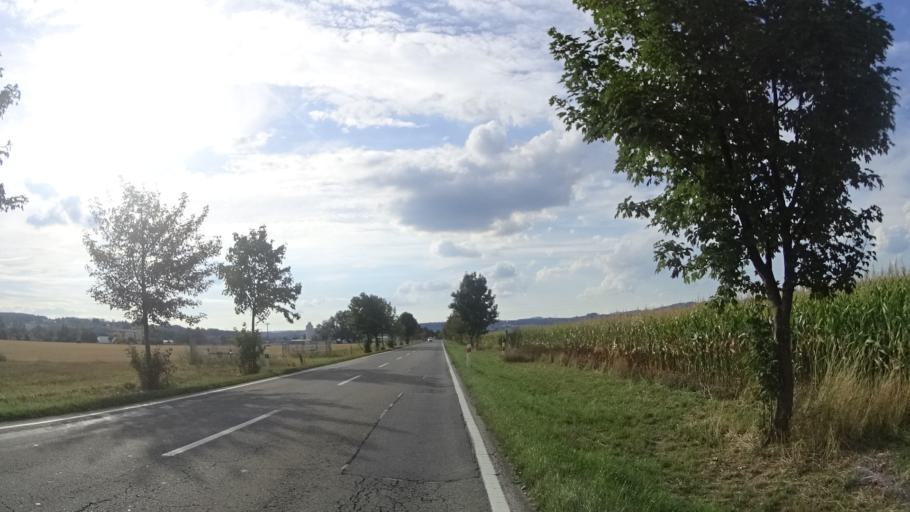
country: CZ
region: Olomoucky
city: Lestina
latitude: 49.8711
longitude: 16.9107
